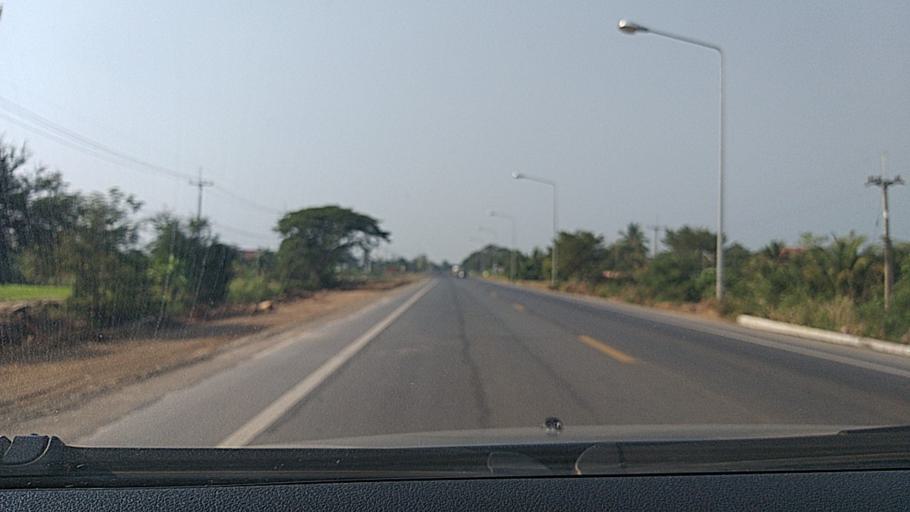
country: TH
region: Sing Buri
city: Phrom Buri
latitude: 14.7733
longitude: 100.4372
